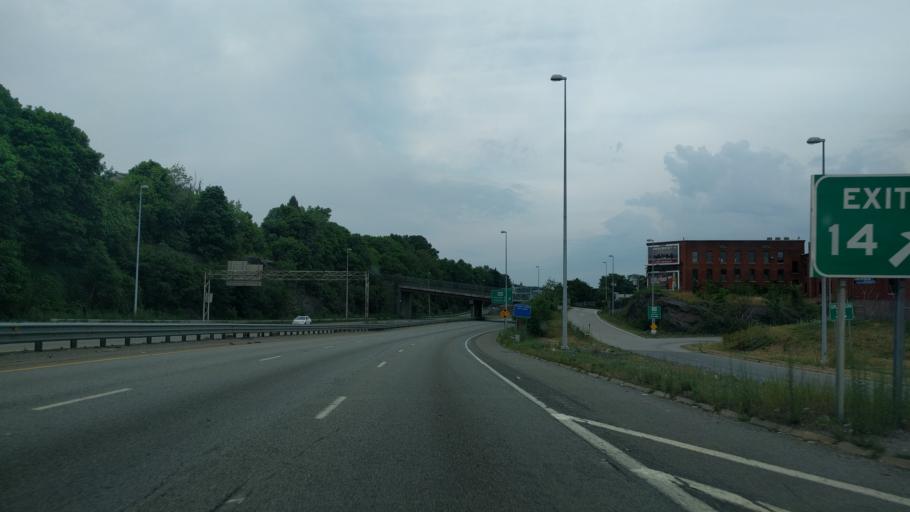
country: US
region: Massachusetts
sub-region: Worcester County
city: Worcester
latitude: 42.2576
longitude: -71.7940
